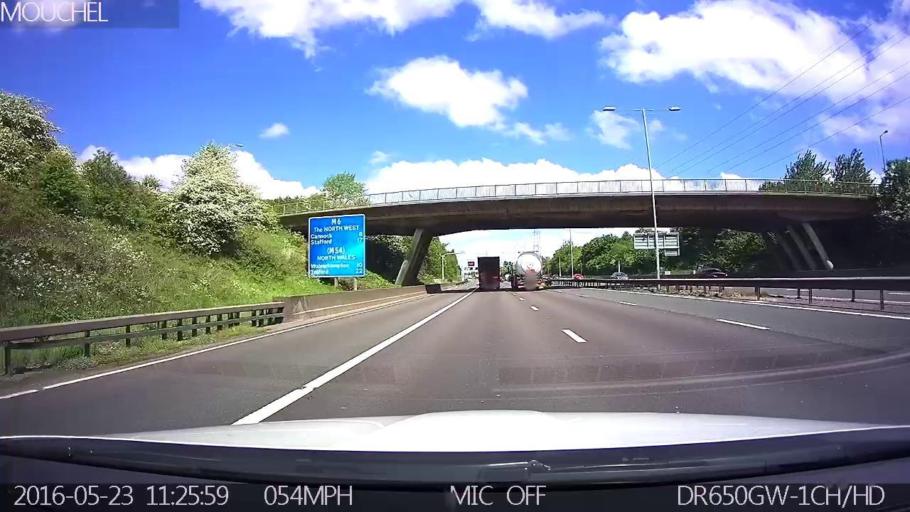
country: GB
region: England
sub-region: Walsall
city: Bloxwich
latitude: 52.5990
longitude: -2.0161
